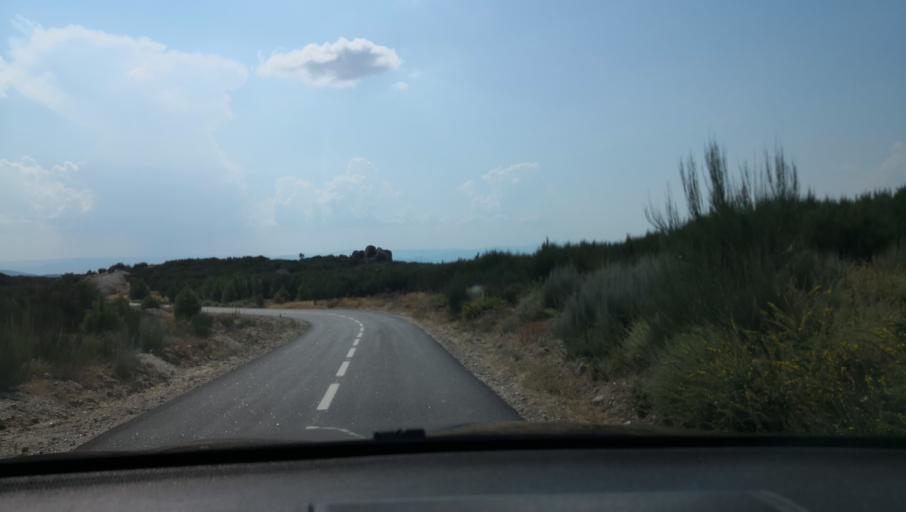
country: PT
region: Vila Real
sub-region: Sabrosa
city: Sabrosa
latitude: 41.2899
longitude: -7.6131
